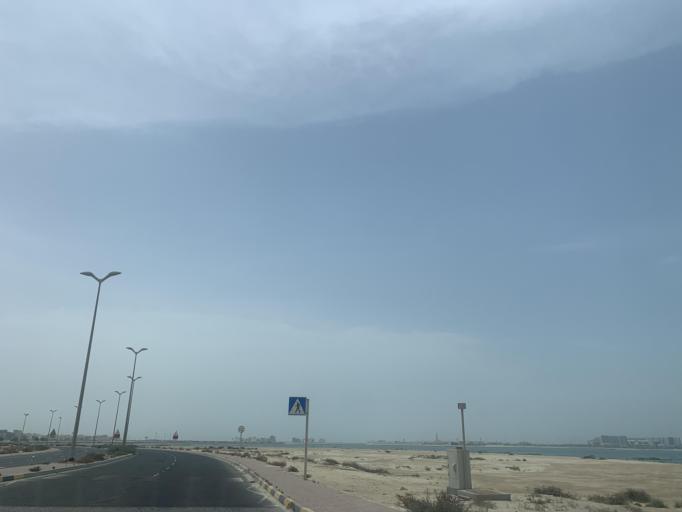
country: BH
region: Muharraq
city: Al Hadd
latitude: 26.2836
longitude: 50.6547
